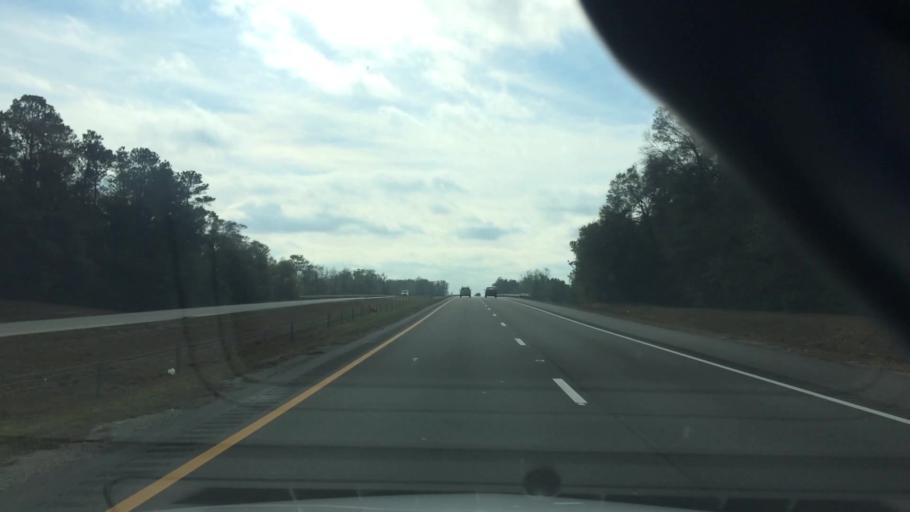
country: US
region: North Carolina
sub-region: New Hanover County
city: Wrightsboro
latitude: 34.3118
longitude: -77.9485
